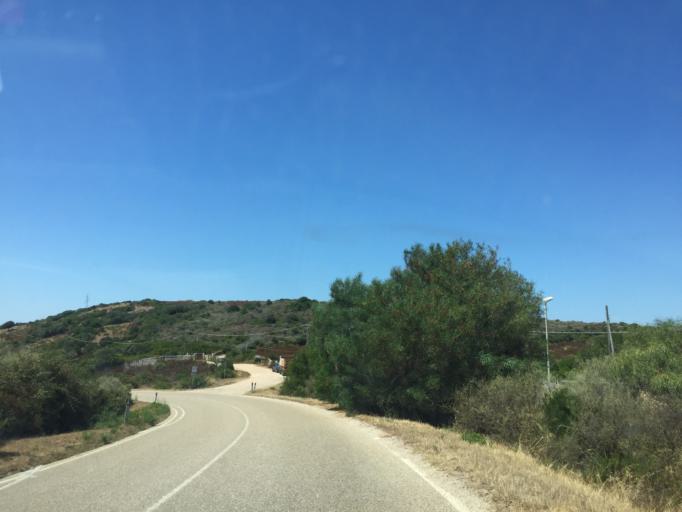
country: IT
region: Sardinia
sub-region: Provincia di Olbia-Tempio
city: Aglientu
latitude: 41.0979
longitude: 9.0996
